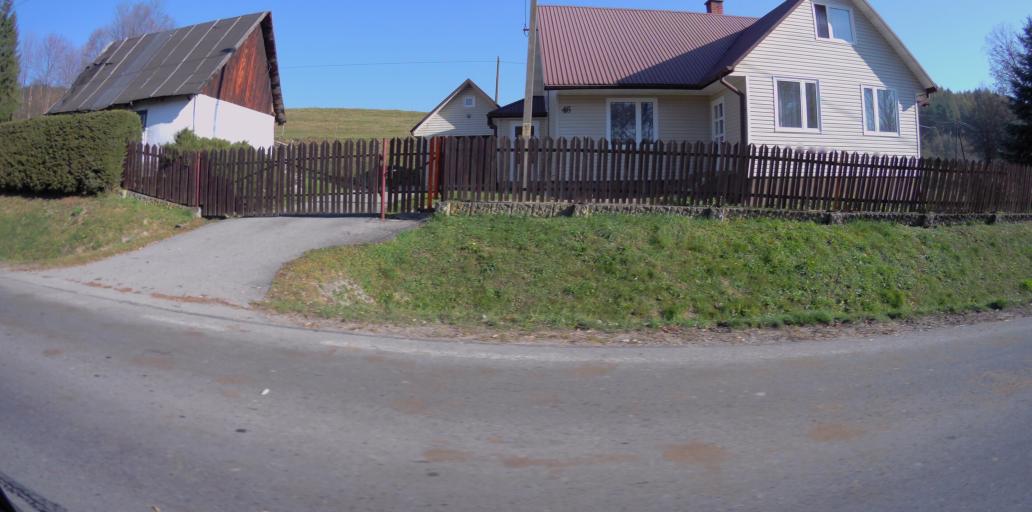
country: PL
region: Subcarpathian Voivodeship
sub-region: Powiat bieszczadzki
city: Ustrzyki Dolne
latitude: 49.4848
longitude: 22.6622
